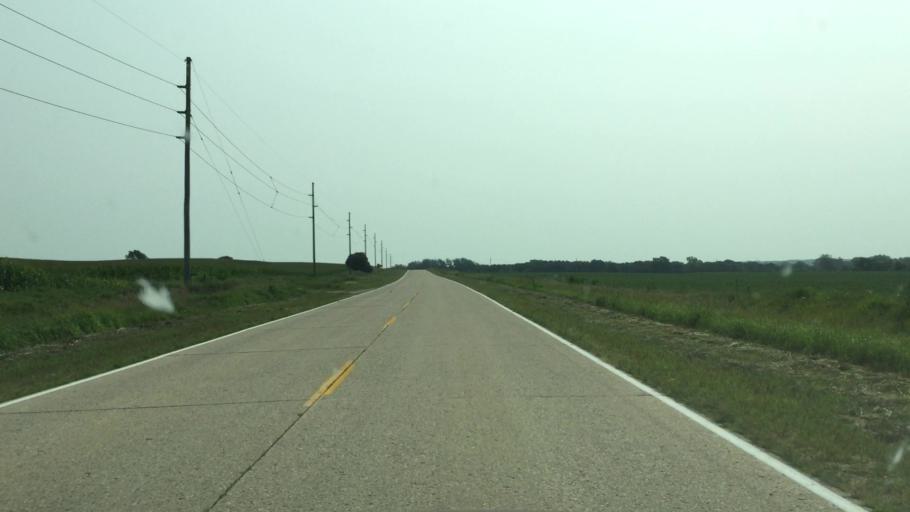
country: US
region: Iowa
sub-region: Dickinson County
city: Milford
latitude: 43.3714
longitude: -95.1910
